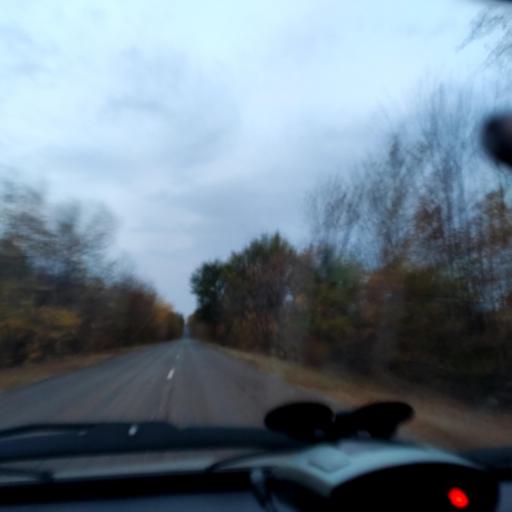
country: RU
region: Belgorod
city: Krasnoye
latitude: 51.2250
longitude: 38.8361
